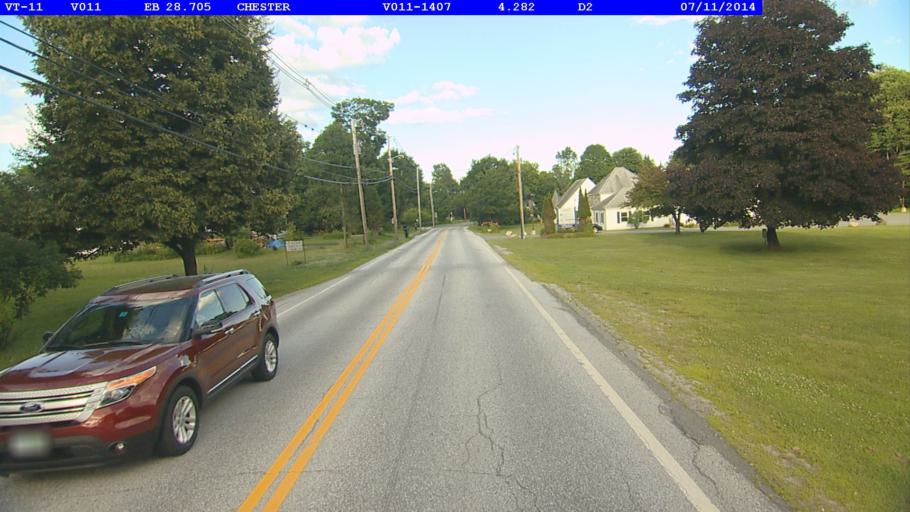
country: US
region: Vermont
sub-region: Windsor County
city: Chester
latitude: 43.2670
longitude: -72.6102
